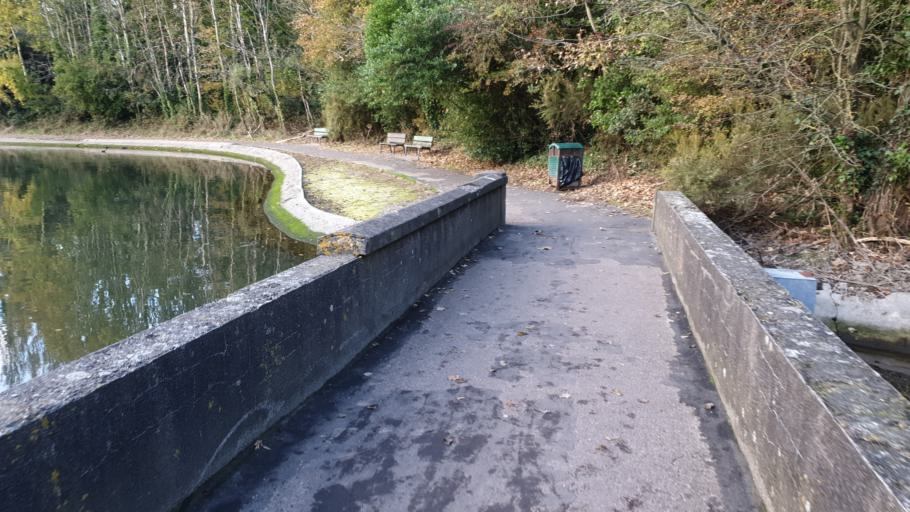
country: IE
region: Munster
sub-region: County Cork
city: Cork
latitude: 51.8994
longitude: -8.4282
